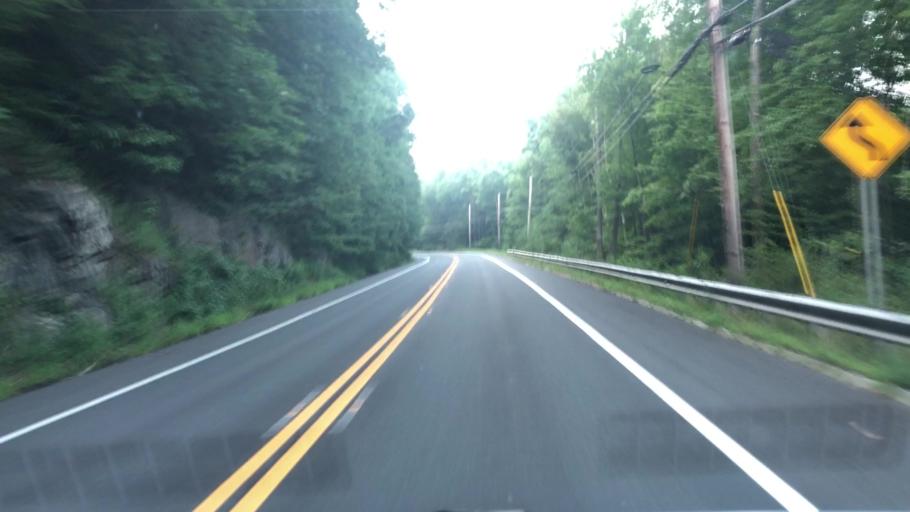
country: US
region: Massachusetts
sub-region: Franklin County
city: Ashfield
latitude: 42.5546
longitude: -72.8051
